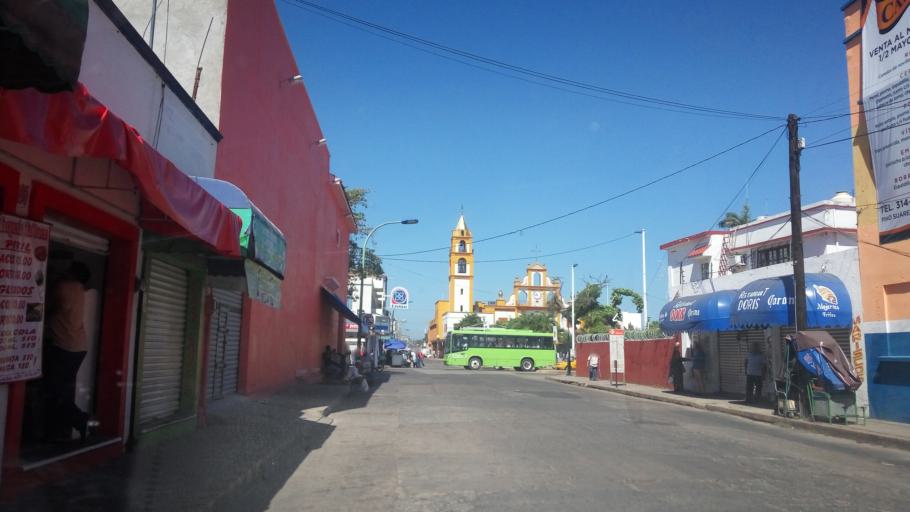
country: MX
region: Tabasco
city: Villahermosa
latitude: 17.9942
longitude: -92.9159
